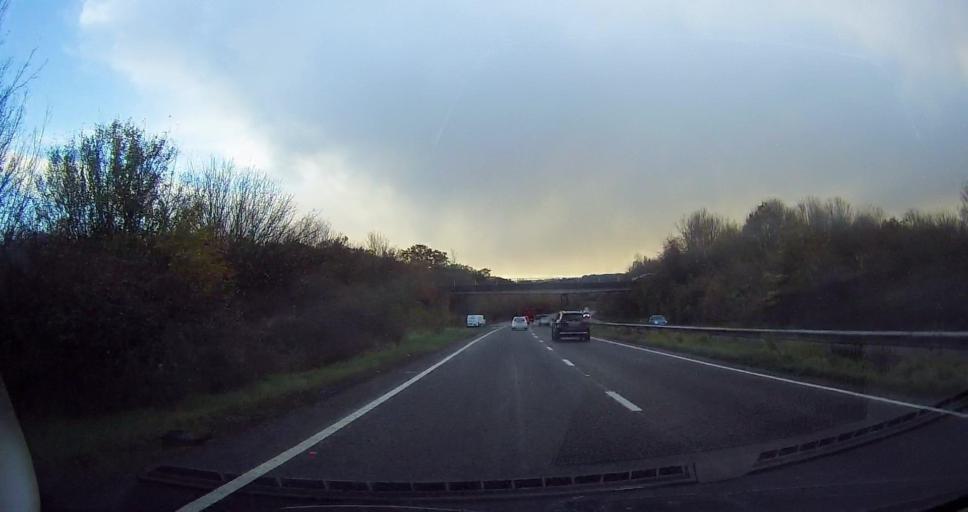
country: GB
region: England
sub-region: West Sussex
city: Hurstpierpoint
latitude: 50.9208
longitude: -0.1926
